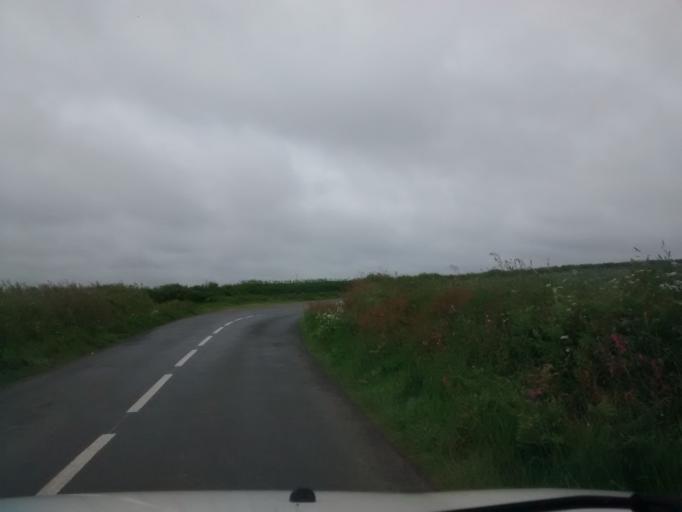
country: FR
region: Brittany
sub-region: Departement des Cotes-d'Armor
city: Plouguiel
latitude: 48.8206
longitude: -3.2587
